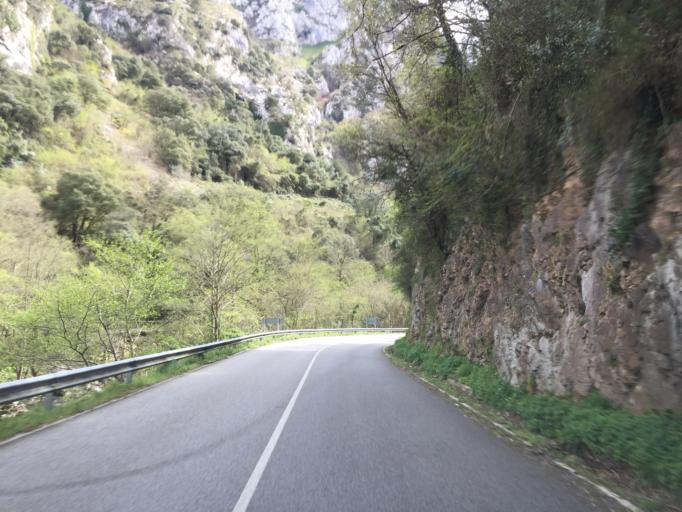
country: ES
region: Asturias
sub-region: Province of Asturias
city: Proaza
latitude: 43.2385
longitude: -6.0307
